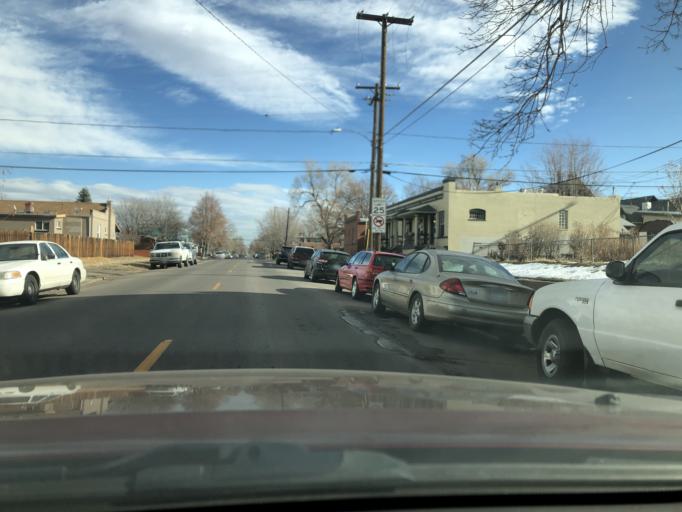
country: US
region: Colorado
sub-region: Denver County
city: Denver
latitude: 39.7582
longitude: -104.9719
